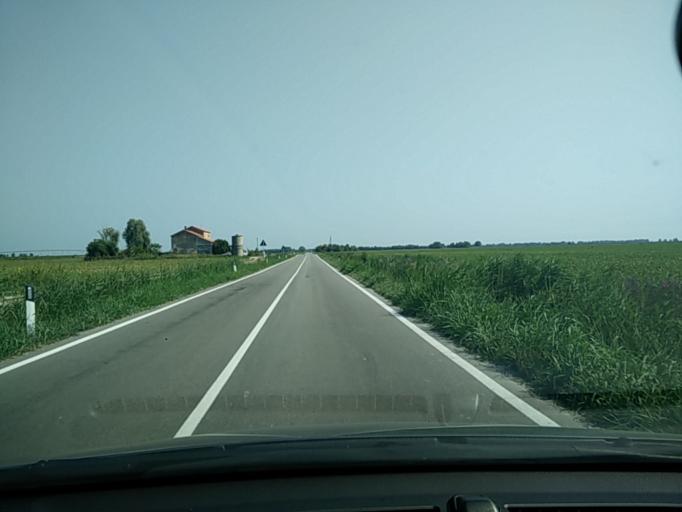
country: IT
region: Veneto
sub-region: Provincia di Venezia
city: La Salute di Livenza
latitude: 45.6425
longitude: 12.8258
